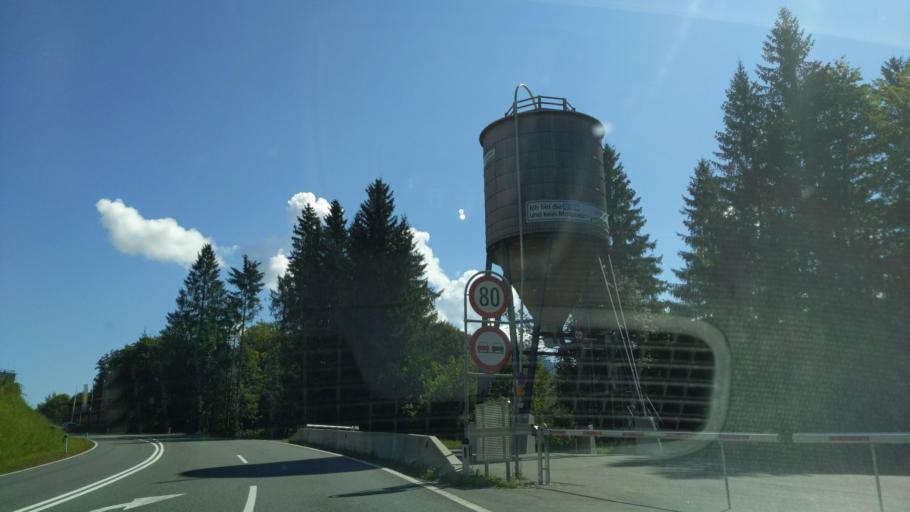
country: AT
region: Tyrol
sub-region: Politischer Bezirk Kitzbuhel
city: Fieberbrunn
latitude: 47.4687
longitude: 12.5657
